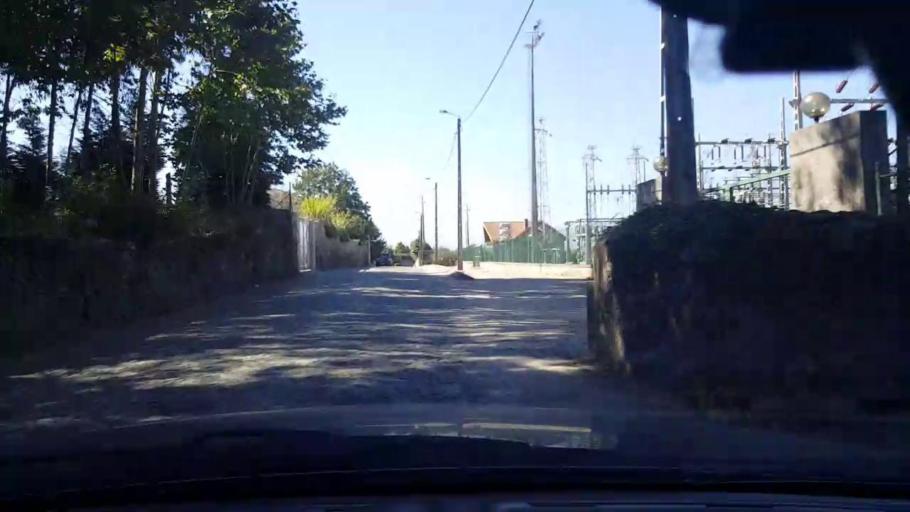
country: PT
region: Porto
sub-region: Maia
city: Gemunde
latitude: 41.2853
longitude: -8.6510
